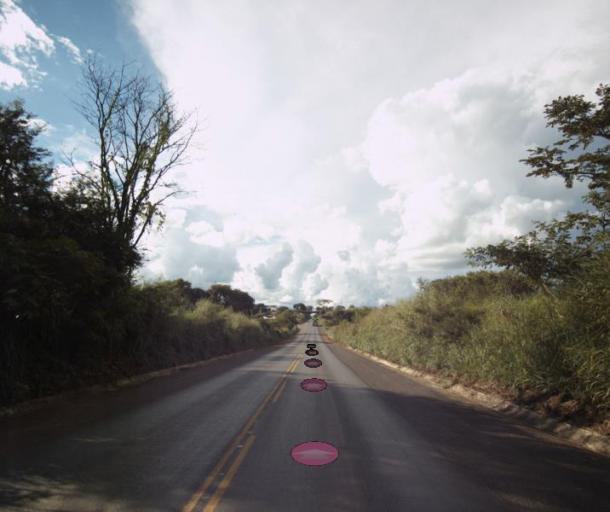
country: BR
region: Goias
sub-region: Rialma
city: Rialma
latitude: -15.3240
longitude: -49.5715
